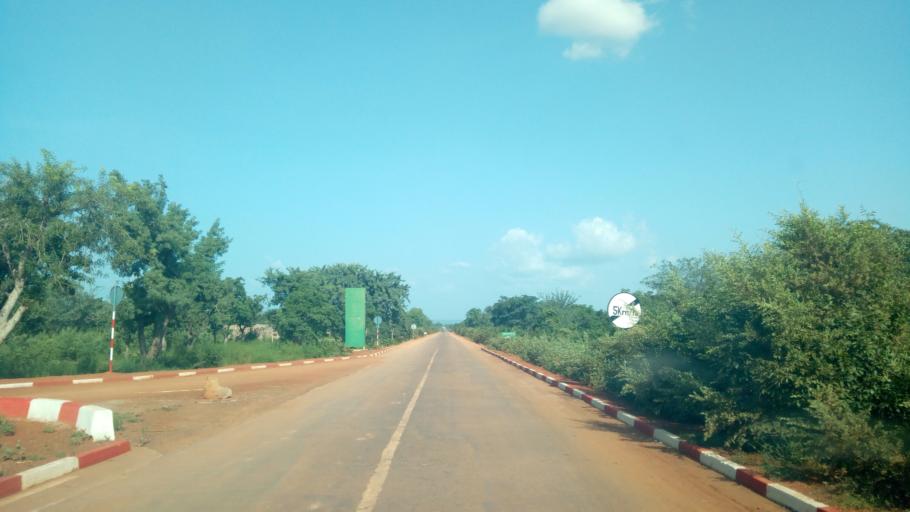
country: ML
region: Sikasso
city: Yorosso
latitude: 12.1851
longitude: -4.8294
